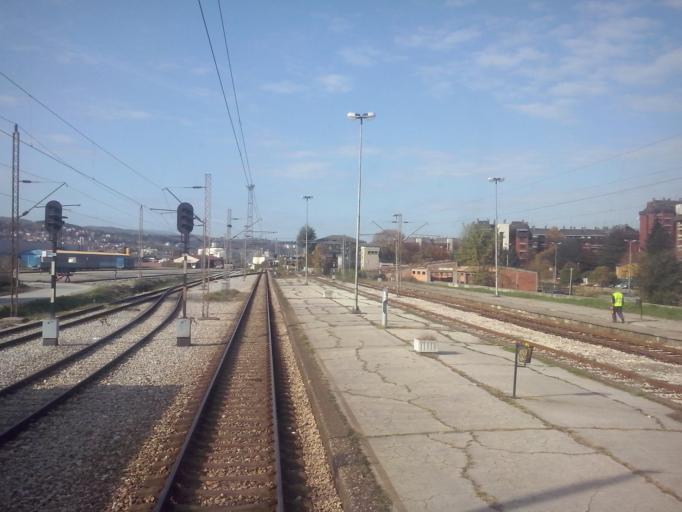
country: RS
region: Central Serbia
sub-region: Kolubarski Okrug
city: Valjevo
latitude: 44.2706
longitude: 19.9070
